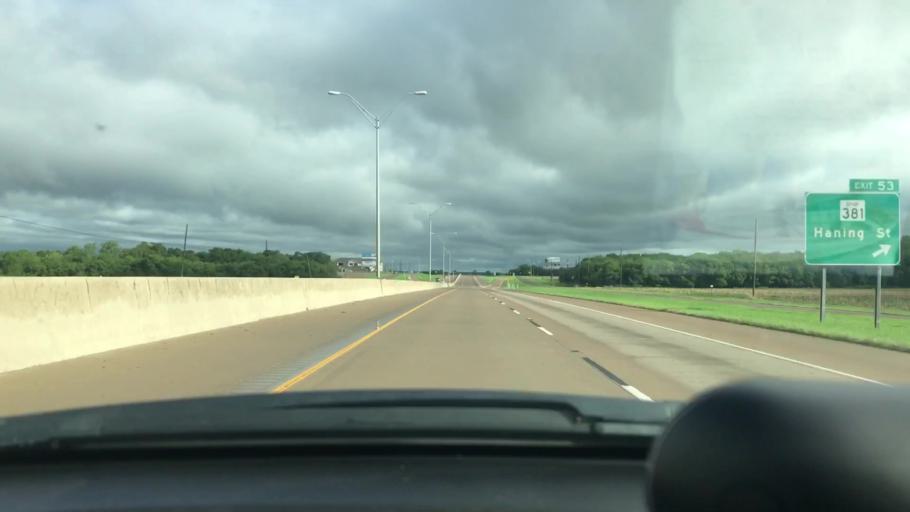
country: US
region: Texas
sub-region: Grayson County
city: Howe
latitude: 33.4873
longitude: -96.6199
